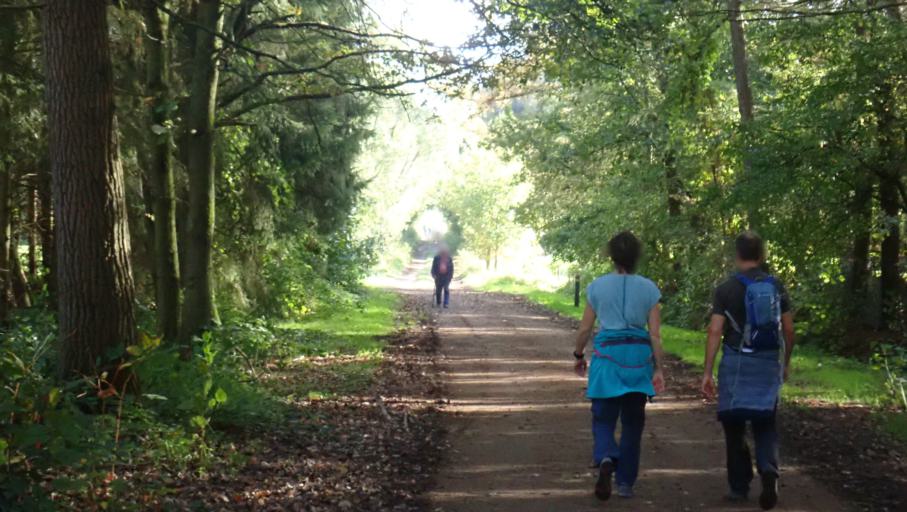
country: BE
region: Flanders
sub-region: Provincie Oost-Vlaanderen
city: Stekene
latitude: 51.1812
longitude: 4.0052
